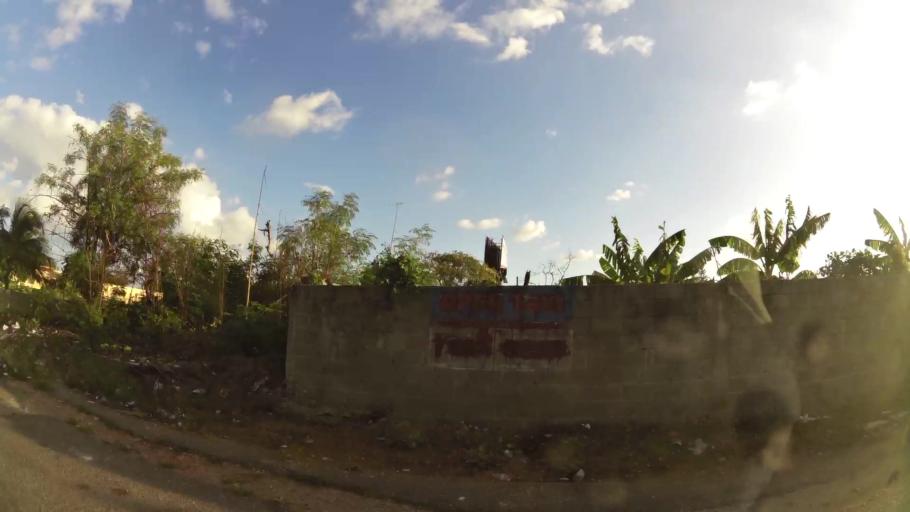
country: DO
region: Santo Domingo
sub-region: Santo Domingo
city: Santo Domingo Este
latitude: 18.4828
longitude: -69.8406
